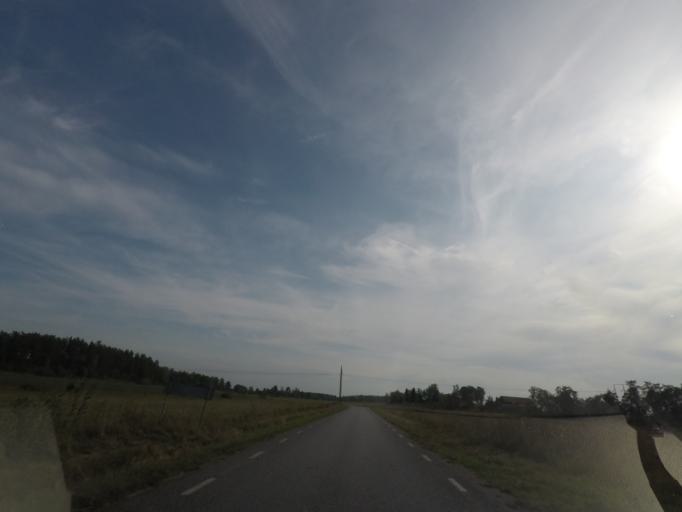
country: SE
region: Vaestmanland
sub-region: Hallstahammars Kommun
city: Kolback
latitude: 59.5310
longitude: 16.1417
